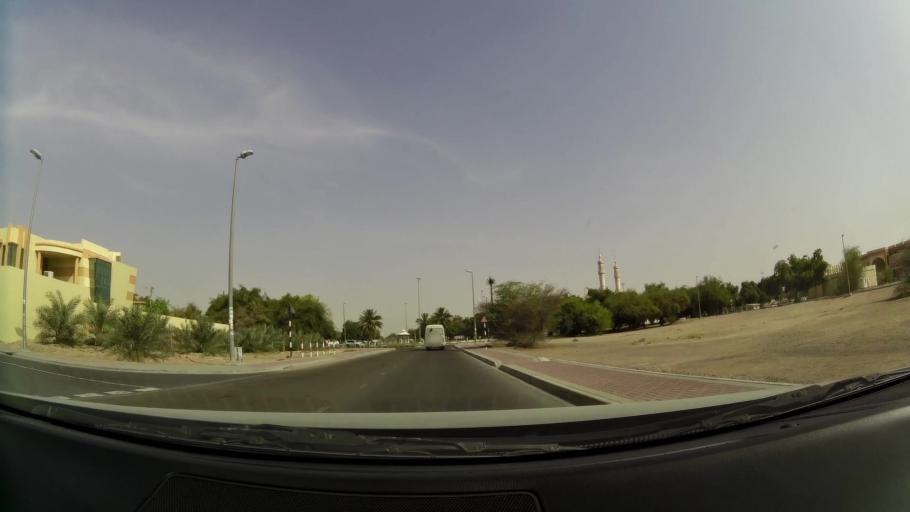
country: AE
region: Abu Dhabi
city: Al Ain
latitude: 24.1499
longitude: 55.6963
